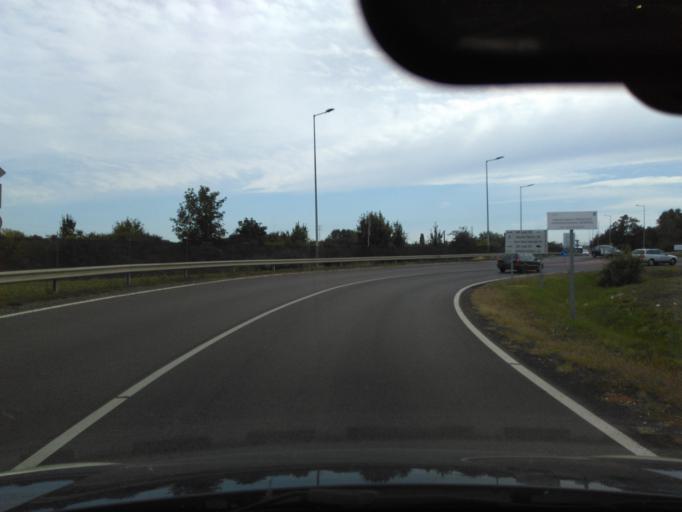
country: HU
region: Heves
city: Hatvan
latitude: 47.6779
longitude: 19.6685
